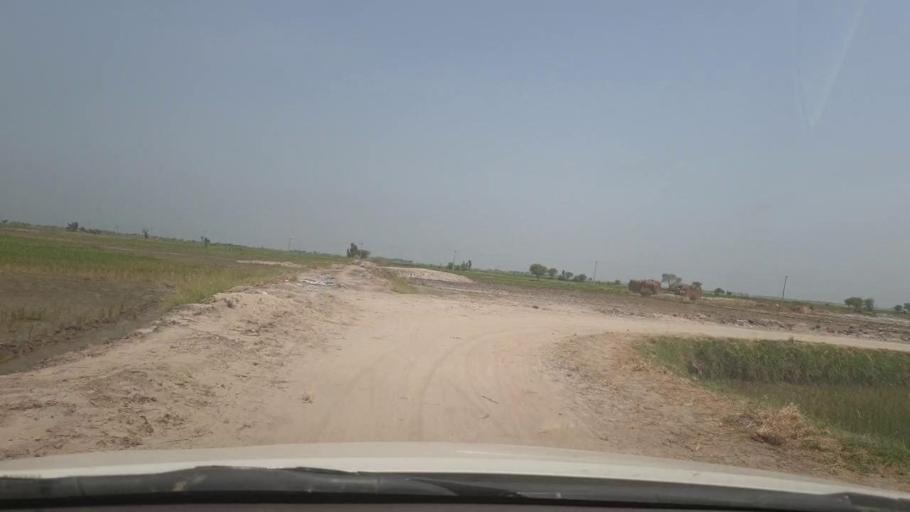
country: PK
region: Sindh
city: Shikarpur
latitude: 28.0424
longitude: 68.5730
